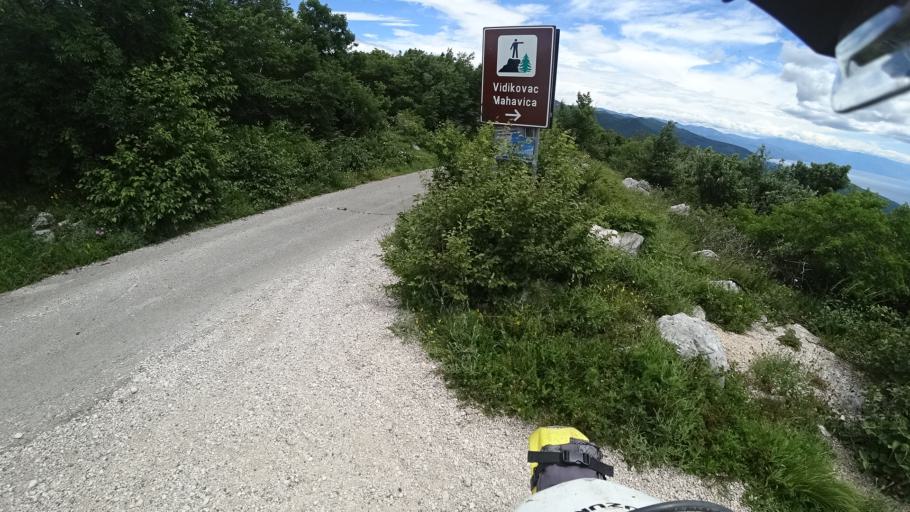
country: HR
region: Primorsko-Goranska
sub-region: Grad Crikvenica
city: Jadranovo
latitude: 45.2417
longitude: 14.6750
